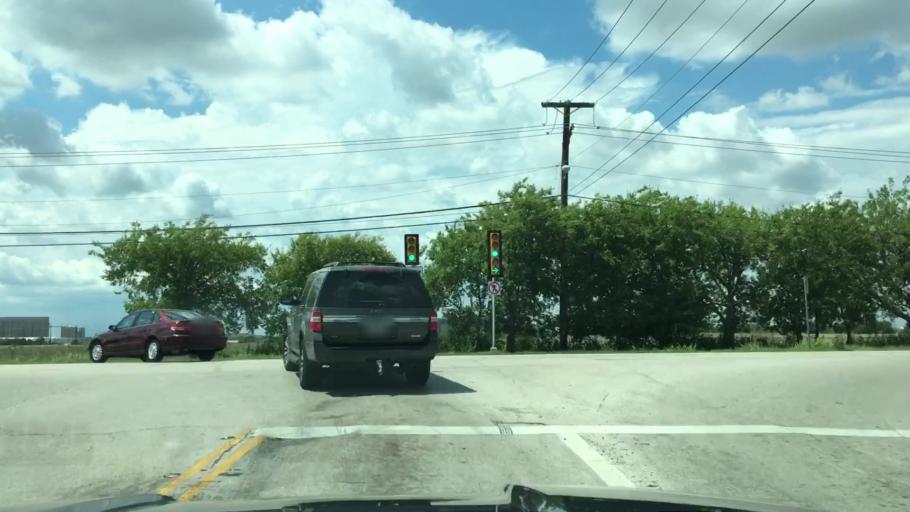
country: US
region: Texas
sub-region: Tarrant County
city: Blue Mound
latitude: 32.8638
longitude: -97.3422
